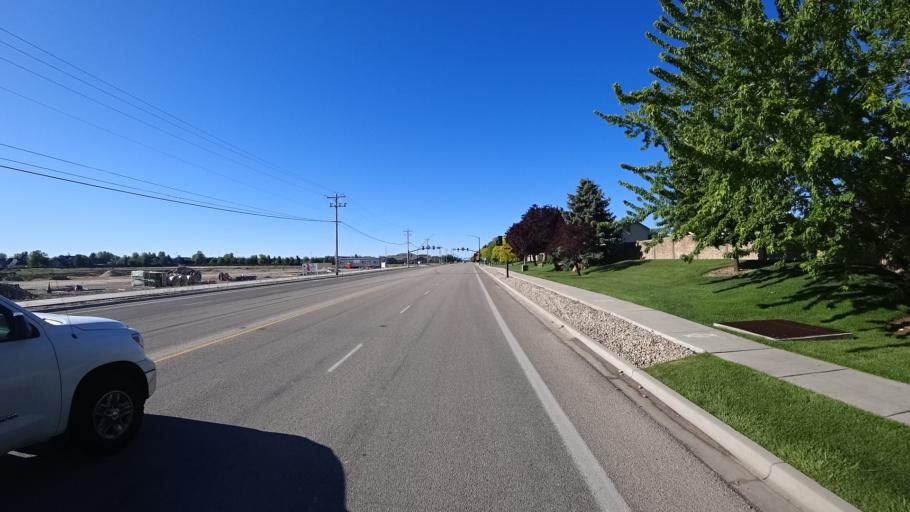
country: US
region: Idaho
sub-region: Ada County
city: Meridian
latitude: 43.6608
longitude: -116.4139
